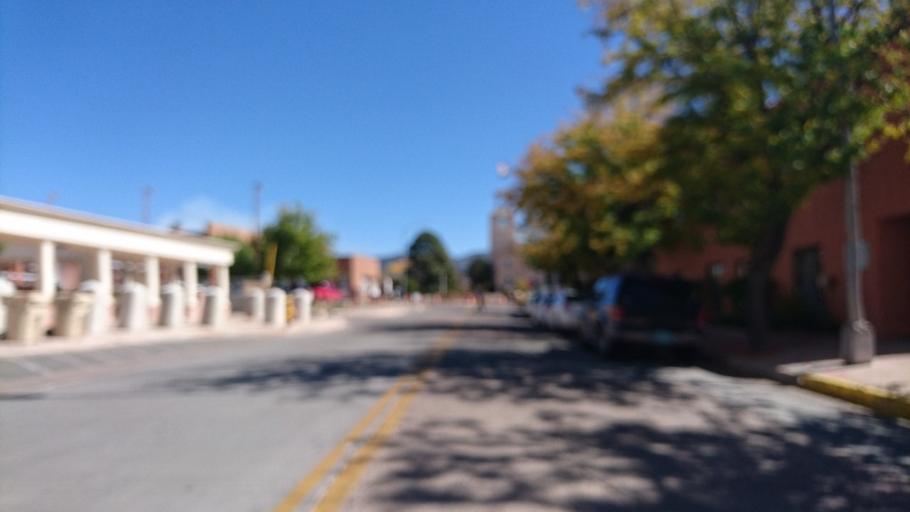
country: US
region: New Mexico
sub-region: Santa Fe County
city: Santa Fe
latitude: 35.6845
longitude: -105.9435
